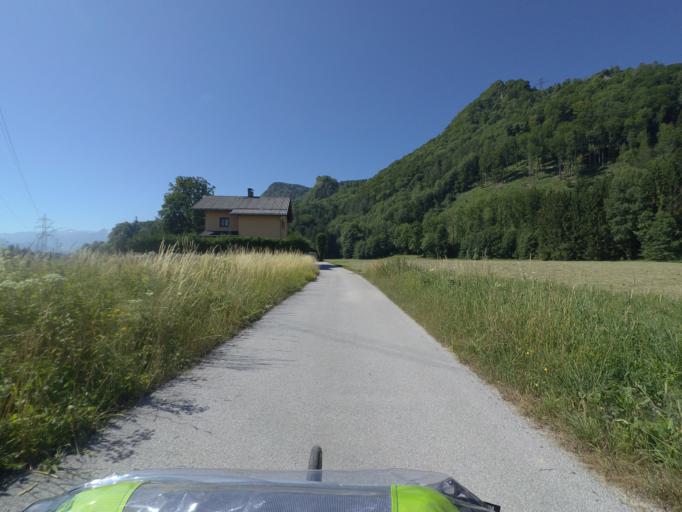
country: DE
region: Bavaria
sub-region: Upper Bavaria
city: Marktschellenberg
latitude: 47.7143
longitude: 13.0608
